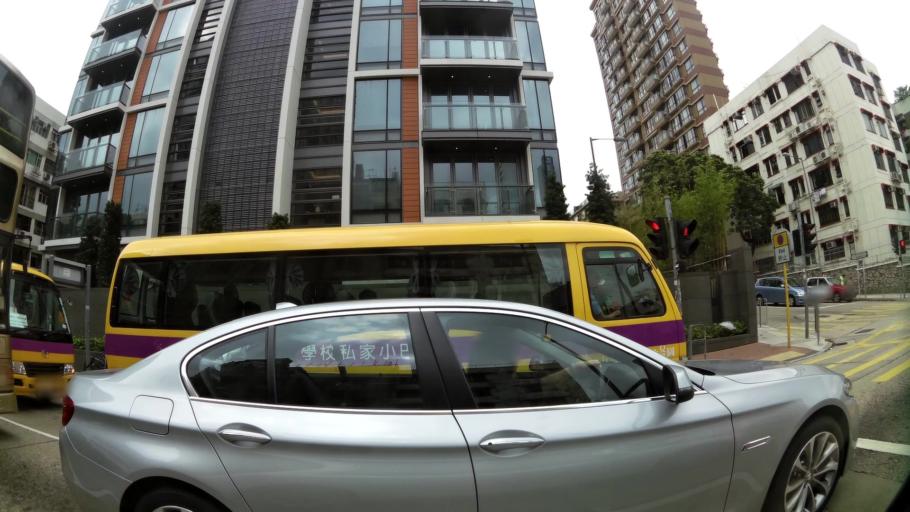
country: HK
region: Kowloon City
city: Kowloon
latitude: 22.3288
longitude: 114.1864
